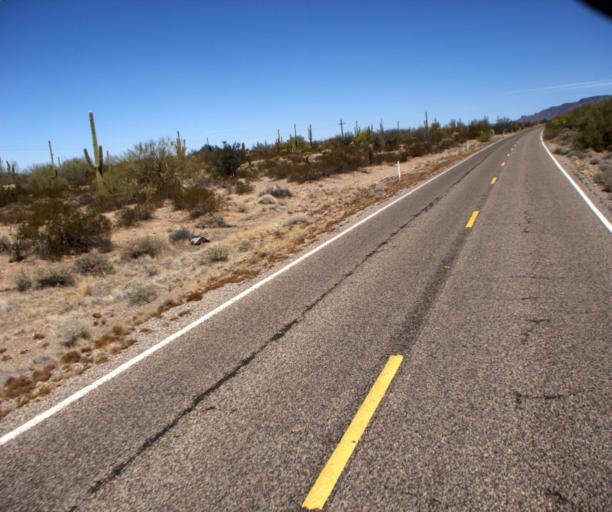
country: US
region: Arizona
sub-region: Pima County
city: Ajo
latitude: 32.2244
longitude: -112.7559
